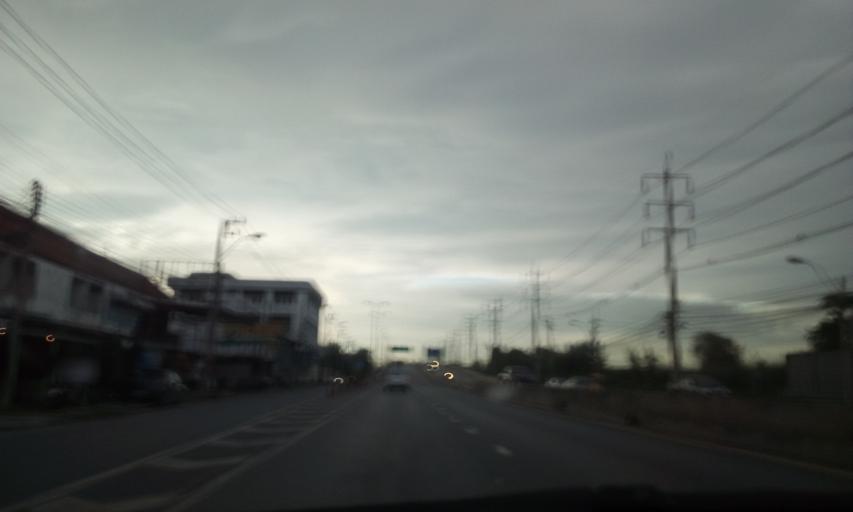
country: TH
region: Phra Nakhon Si Ayutthaya
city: Ban Bang Kadi Pathum Thani
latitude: 13.9633
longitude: 100.5506
